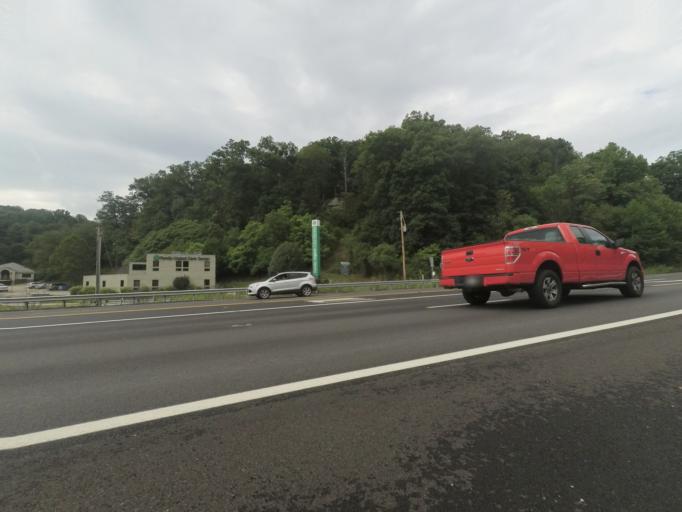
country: US
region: West Virginia
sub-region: Cabell County
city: Huntington
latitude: 38.3961
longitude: -82.4503
